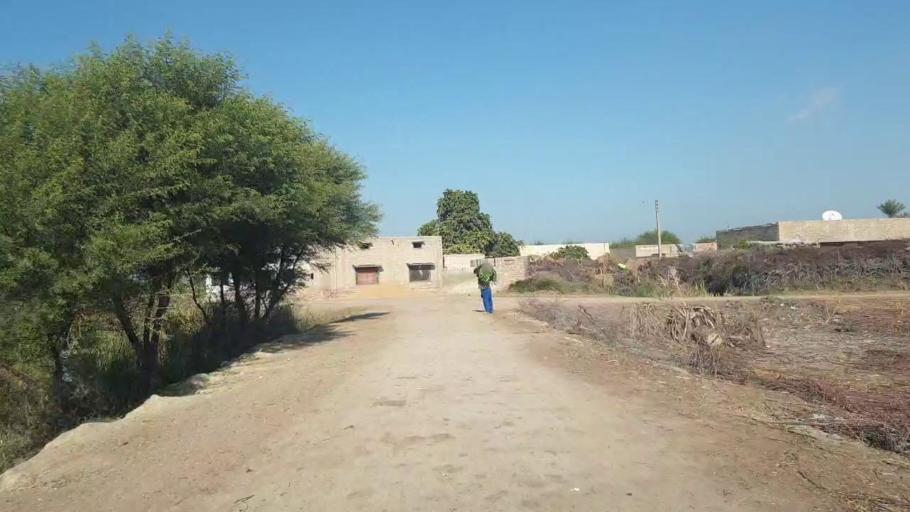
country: PK
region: Sindh
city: Shahdadpur
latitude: 25.9032
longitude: 68.5520
